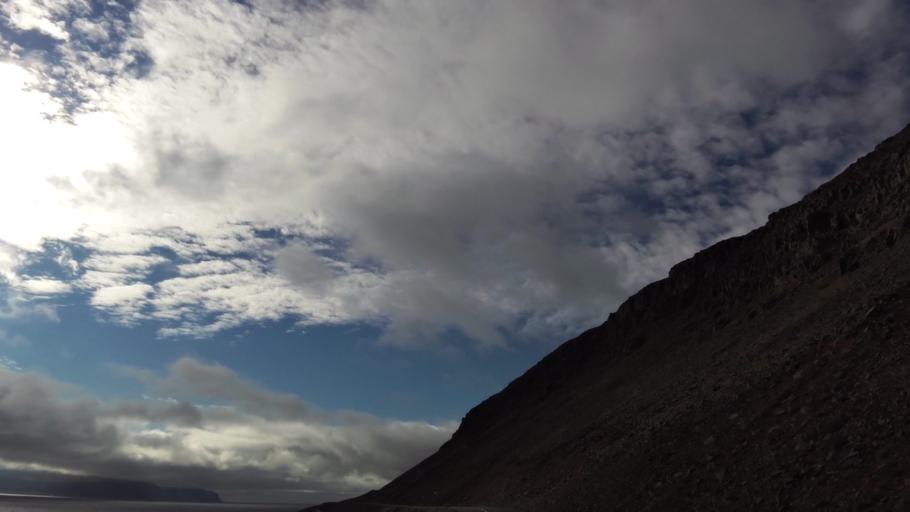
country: IS
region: West
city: Olafsvik
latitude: 65.5785
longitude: -23.9483
